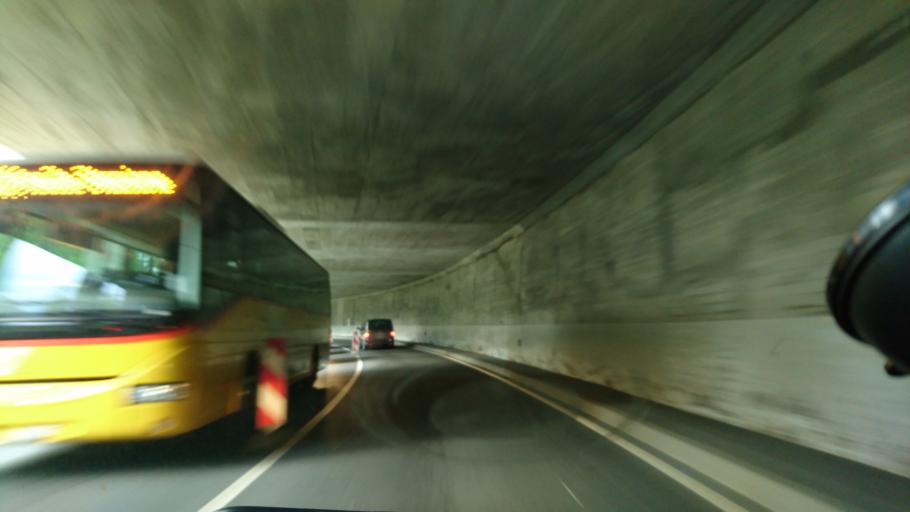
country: CH
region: Valais
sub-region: Brig District
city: Brig
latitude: 46.2714
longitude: 8.0406
